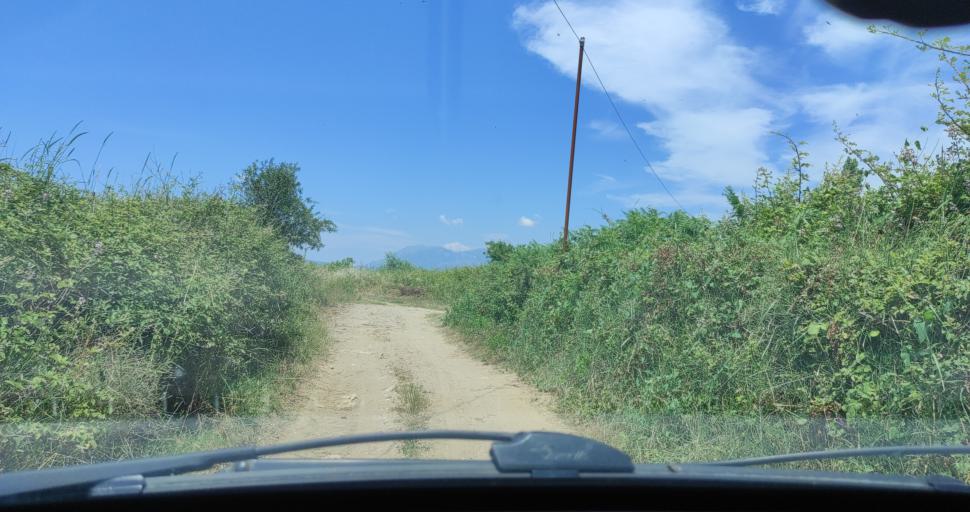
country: AL
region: Shkoder
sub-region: Rrethi i Shkodres
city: Velipoje
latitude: 41.8842
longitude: 19.3886
